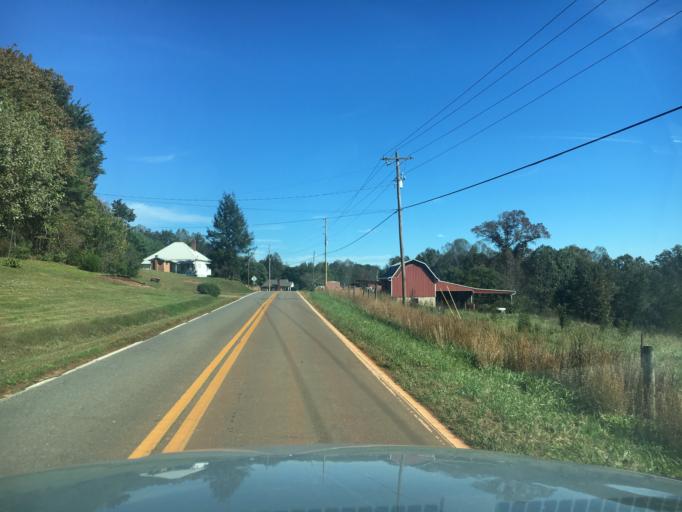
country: US
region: North Carolina
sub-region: Burke County
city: Salem
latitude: 35.7154
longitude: -81.7364
